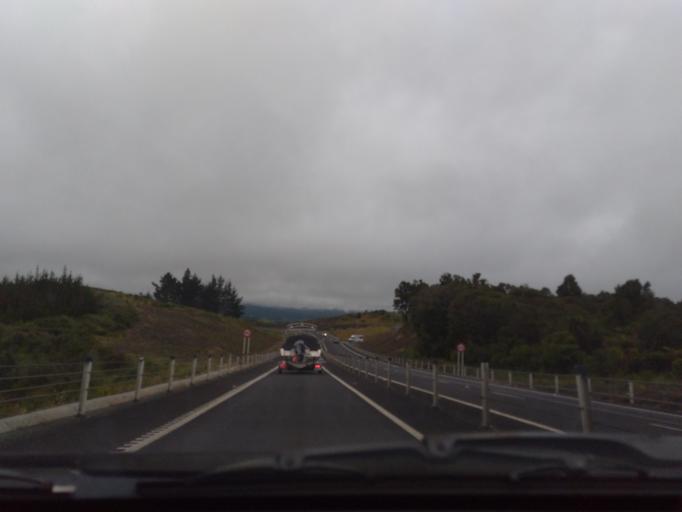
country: NZ
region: Northland
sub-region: Whangarei
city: Ruakaka
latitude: -36.0572
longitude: 174.4263
